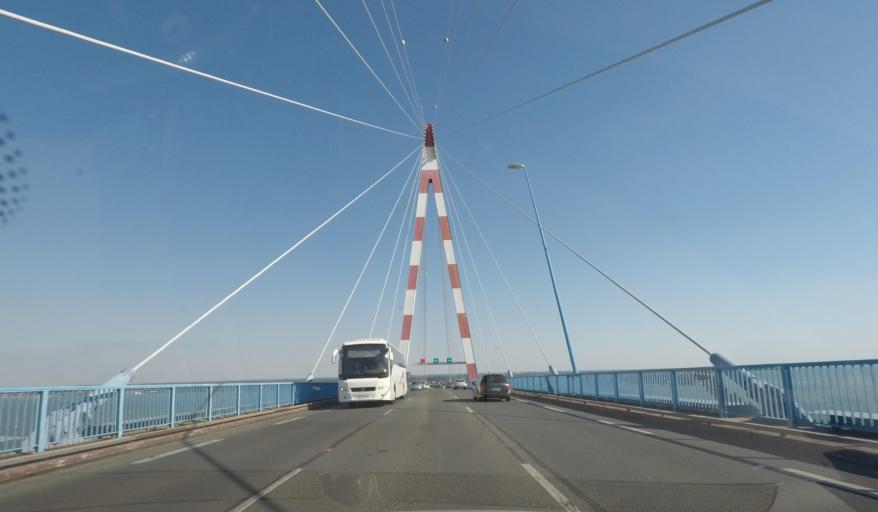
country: FR
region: Pays de la Loire
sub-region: Departement de la Loire-Atlantique
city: Saint-Nazaire
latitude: 47.2843
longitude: -2.1699
